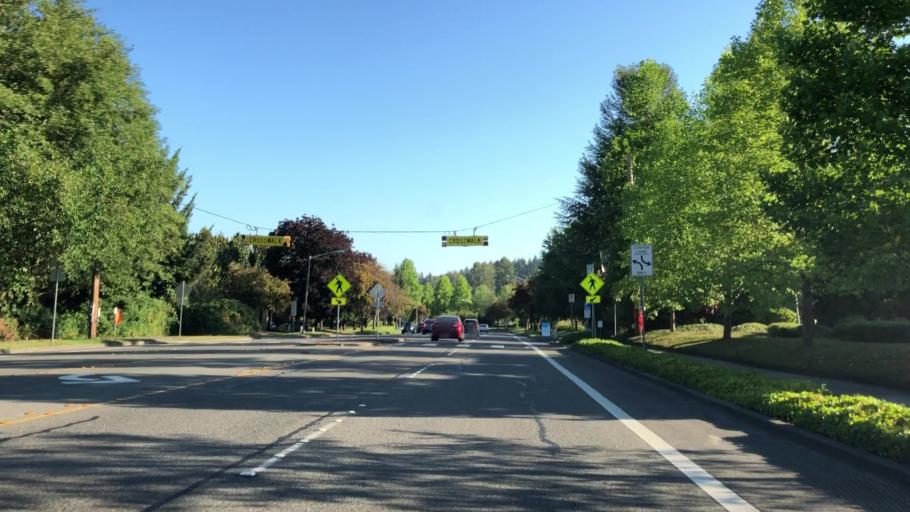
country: US
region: Washington
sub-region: King County
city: Woodinville
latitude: 47.7612
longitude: -122.1767
